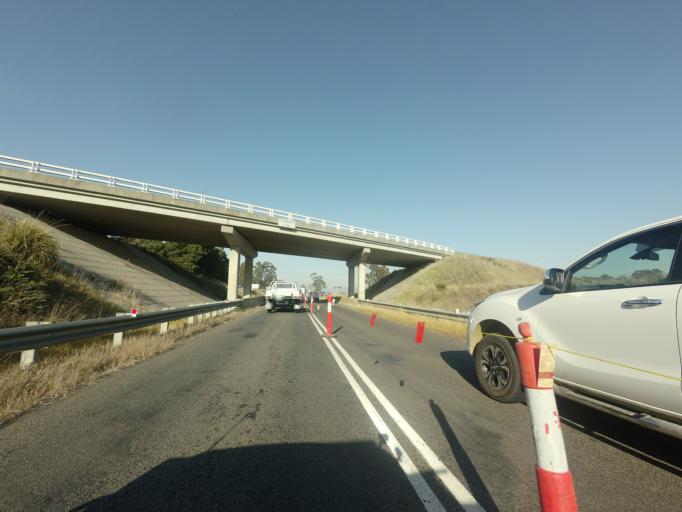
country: AU
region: Tasmania
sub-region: Northern Midlands
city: Longford
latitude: -41.5530
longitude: 146.9890
